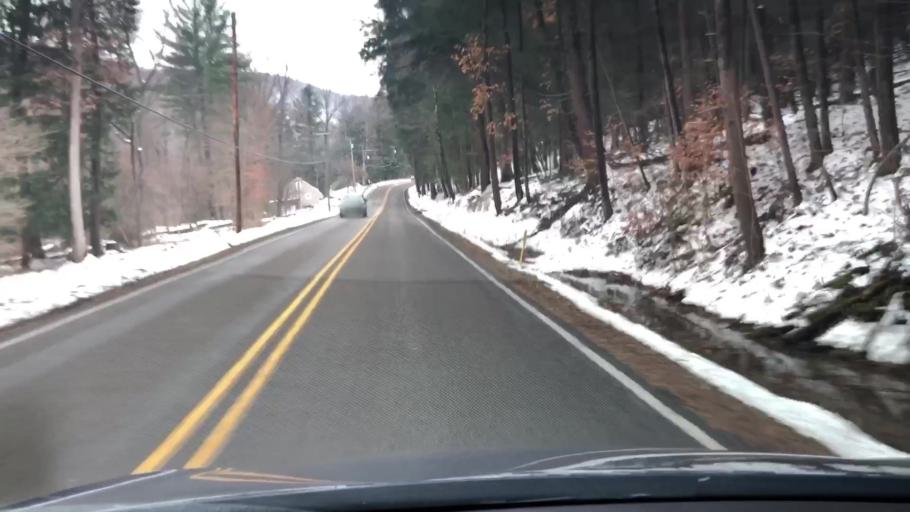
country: US
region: Pennsylvania
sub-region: Elk County
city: Saint Marys
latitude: 41.3054
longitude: -78.4004
